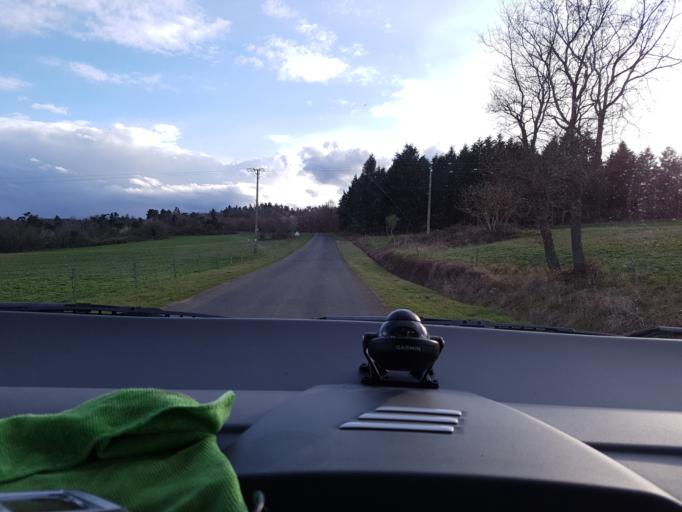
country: FR
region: Auvergne
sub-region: Departement de la Haute-Loire
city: Lempdes-sur-Allagnon
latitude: 45.3406
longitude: 3.2320
